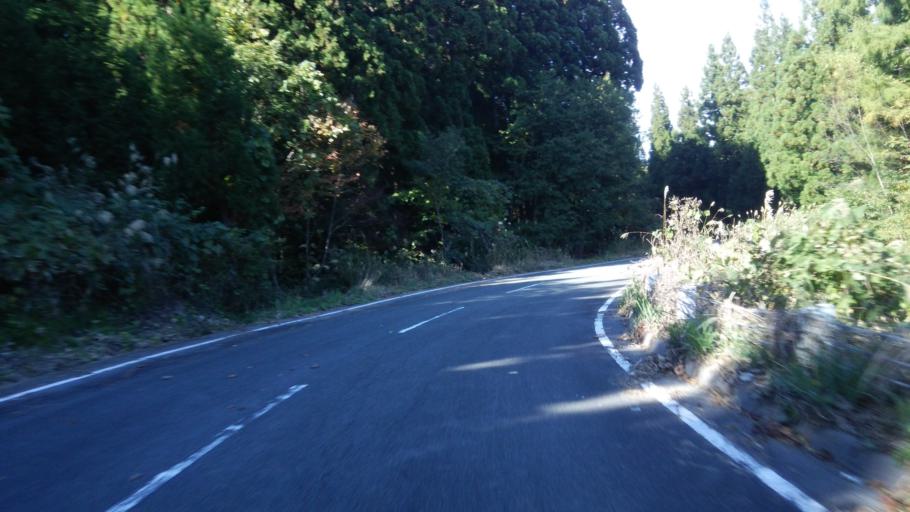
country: JP
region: Fukushima
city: Kitakata
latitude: 37.4246
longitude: 139.7837
